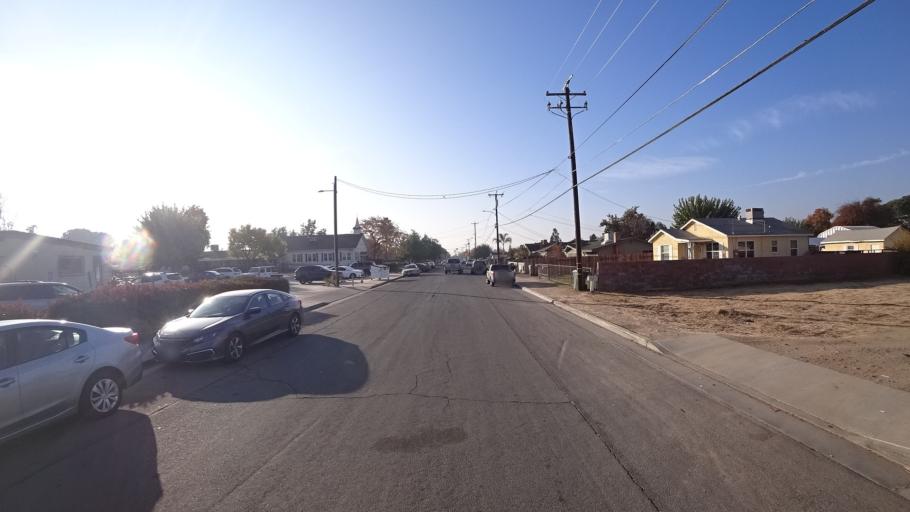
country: US
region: California
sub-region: Kern County
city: Greenacres
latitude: 35.3820
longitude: -119.1171
